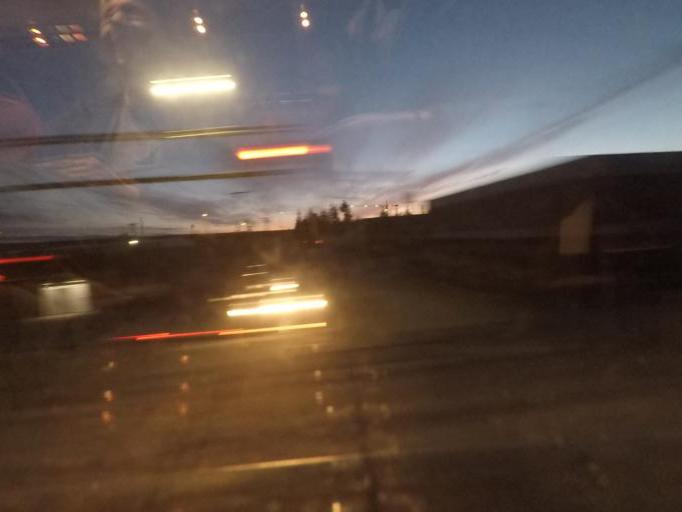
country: US
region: Washington
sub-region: Snohomish County
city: Marysville
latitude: 48.0491
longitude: -122.1805
